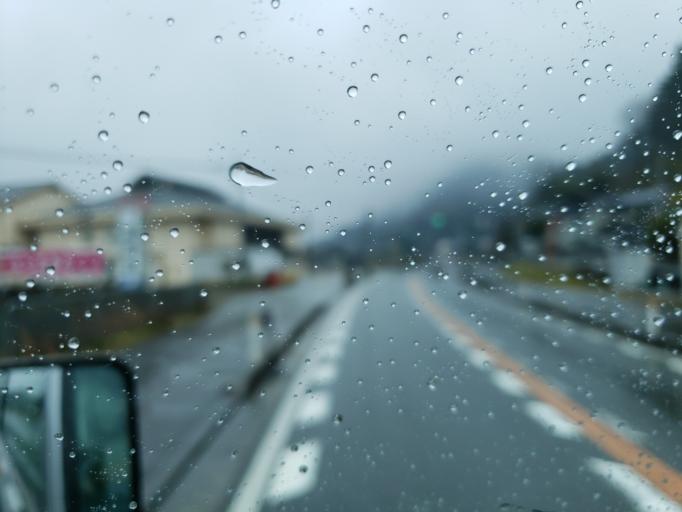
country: JP
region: Hyogo
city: Toyooka
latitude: 35.3914
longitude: 134.7367
